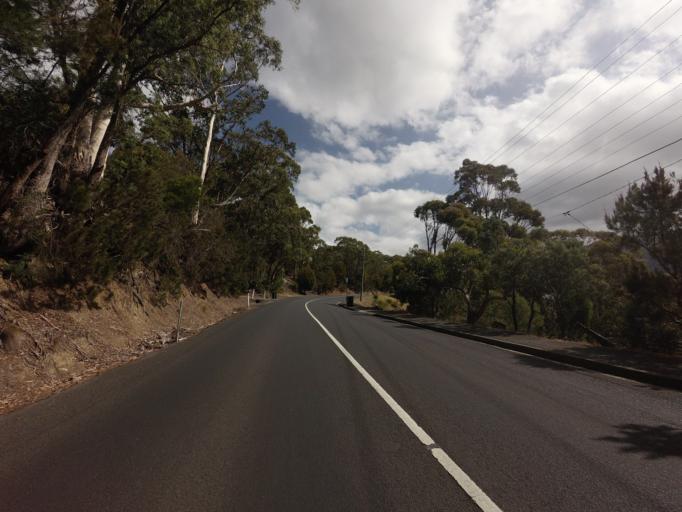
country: AU
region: Tasmania
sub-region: Hobart
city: Dynnyrne
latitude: -42.8997
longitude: 147.2994
